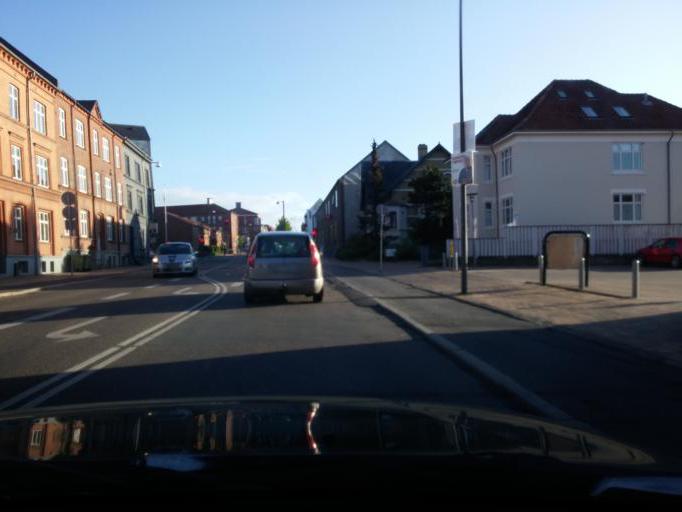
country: DK
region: South Denmark
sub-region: Odense Kommune
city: Odense
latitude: 55.4049
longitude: 10.3929
